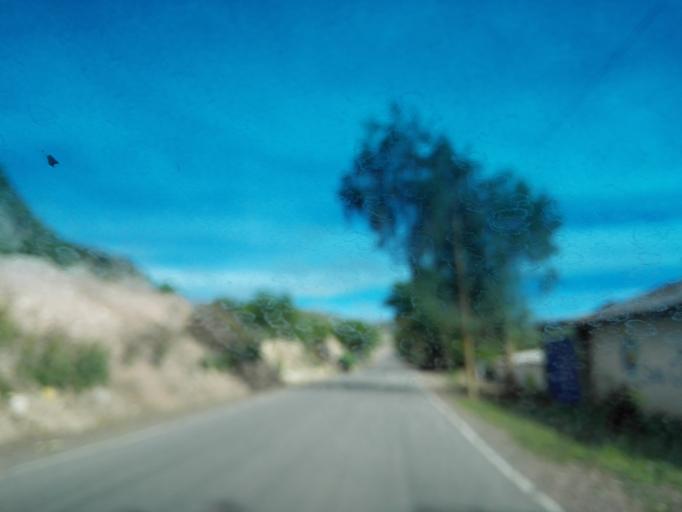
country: PE
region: Ayacucho
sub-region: Provincia de Huamanga
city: Pacaycasa
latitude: -13.0791
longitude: -74.2305
